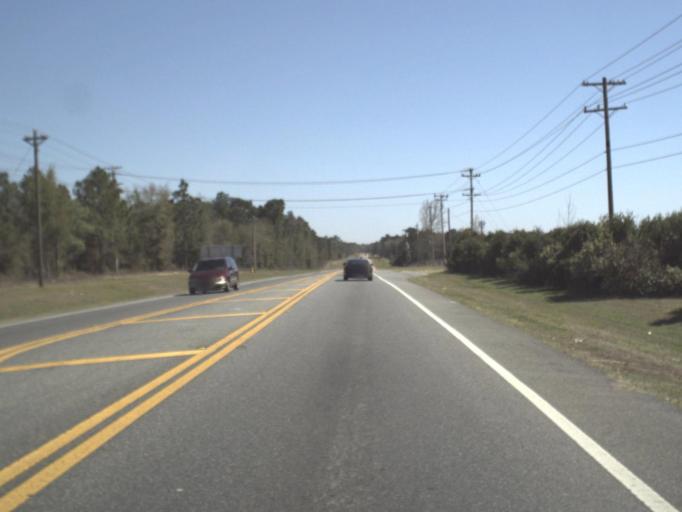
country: US
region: Florida
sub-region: Leon County
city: Tallahassee
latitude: 30.3928
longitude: -84.3205
